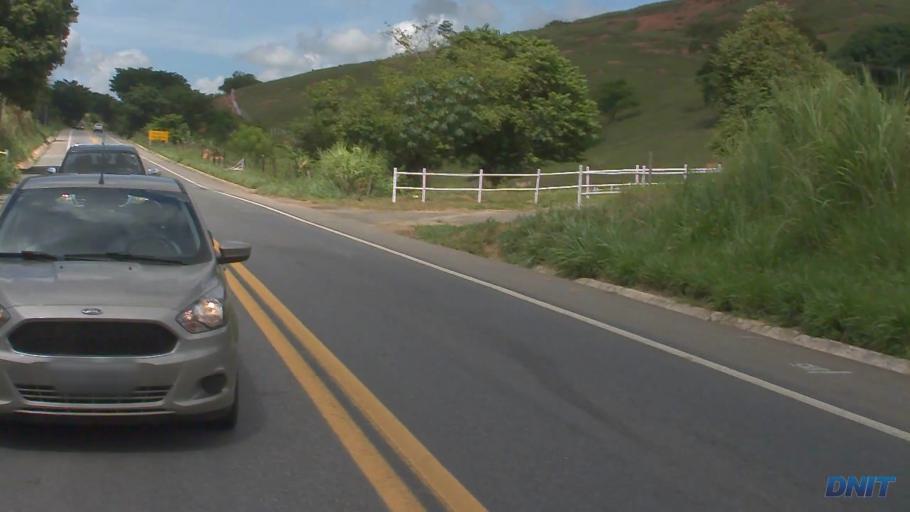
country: BR
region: Minas Gerais
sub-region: Governador Valadares
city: Governador Valadares
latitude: -18.9639
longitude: -42.0791
